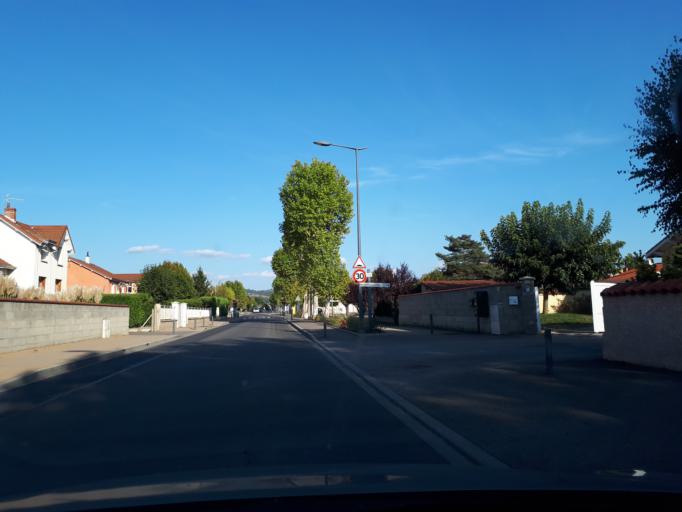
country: FR
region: Rhone-Alpes
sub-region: Departement de la Loire
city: Saint-Andre-le-Puy
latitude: 45.6451
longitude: 4.2571
